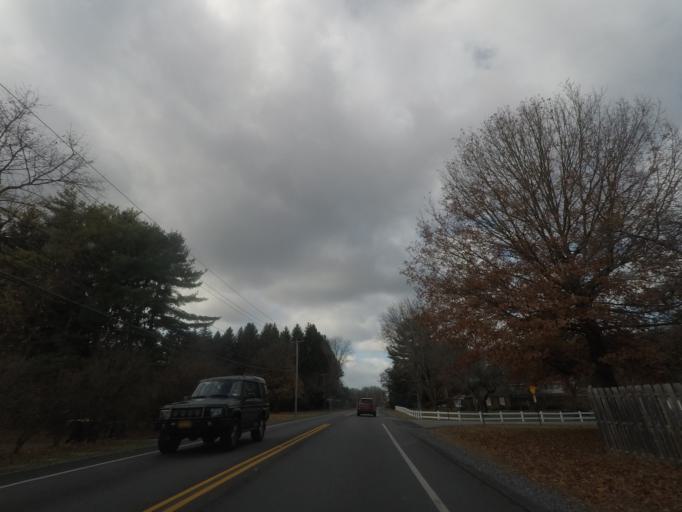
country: US
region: New York
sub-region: Saratoga County
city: Ballston Spa
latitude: 43.0115
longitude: -73.7912
